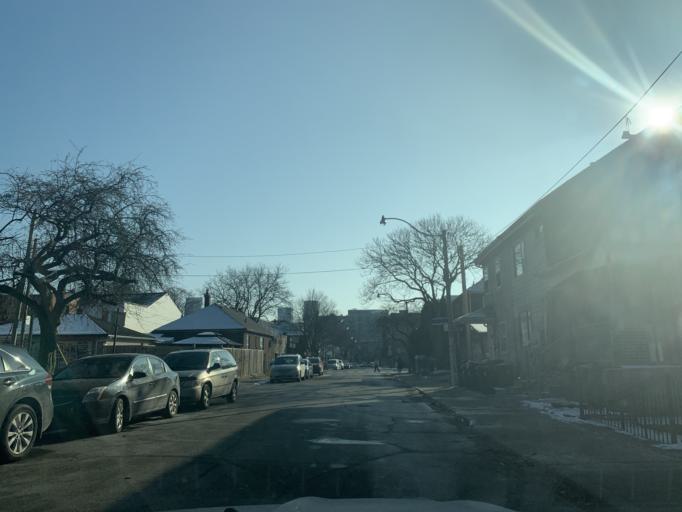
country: CA
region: Ontario
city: Toronto
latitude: 43.6500
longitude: -79.4030
